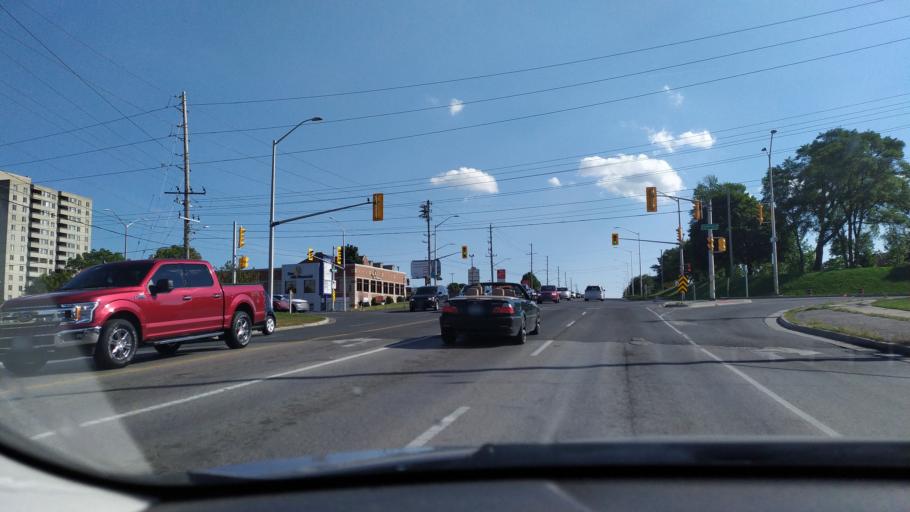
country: CA
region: Ontario
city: London
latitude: 42.9573
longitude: -81.2607
